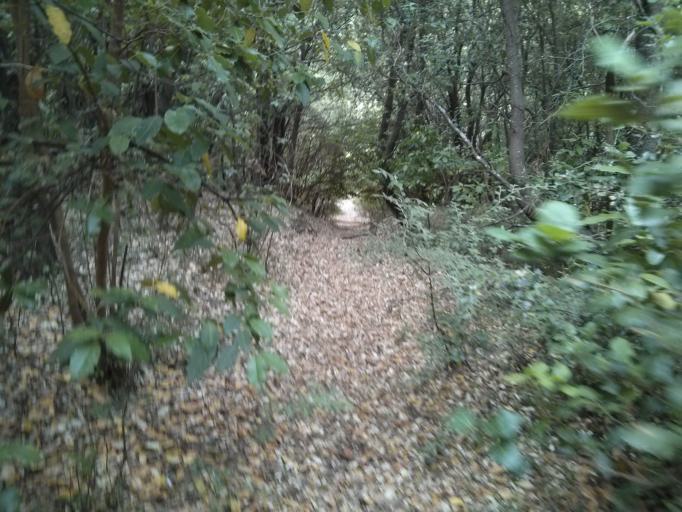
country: FR
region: Pays de la Loire
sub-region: Departement de la Vendee
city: Saint-Jean-de-Monts
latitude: 46.7931
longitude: -2.0721
